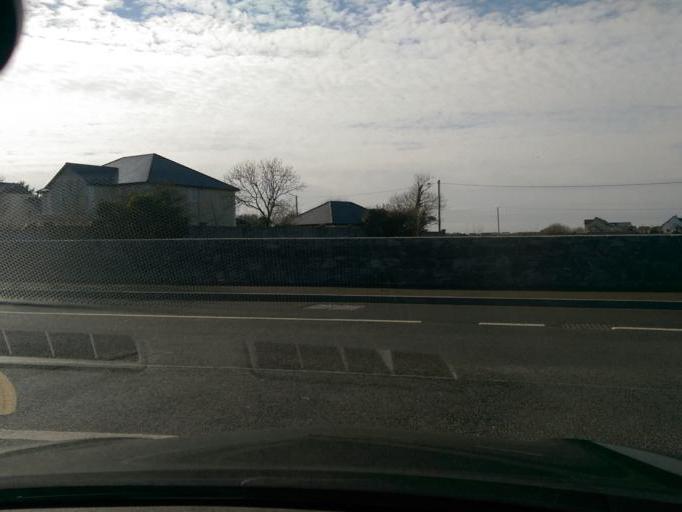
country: IE
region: Connaught
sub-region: County Galway
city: Oranmore
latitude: 53.2591
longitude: -8.9331
